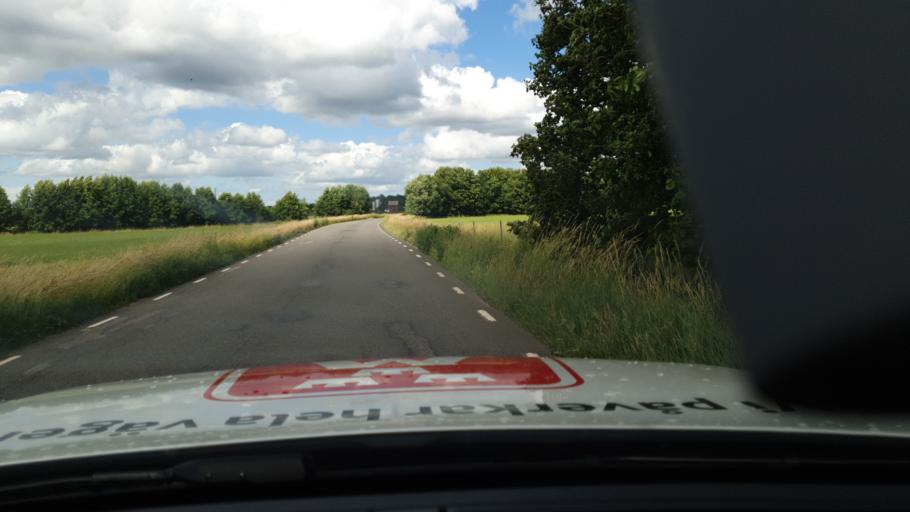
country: SE
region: Vaestra Goetaland
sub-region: Skara Kommun
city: Axvall
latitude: 58.3622
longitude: 13.6279
